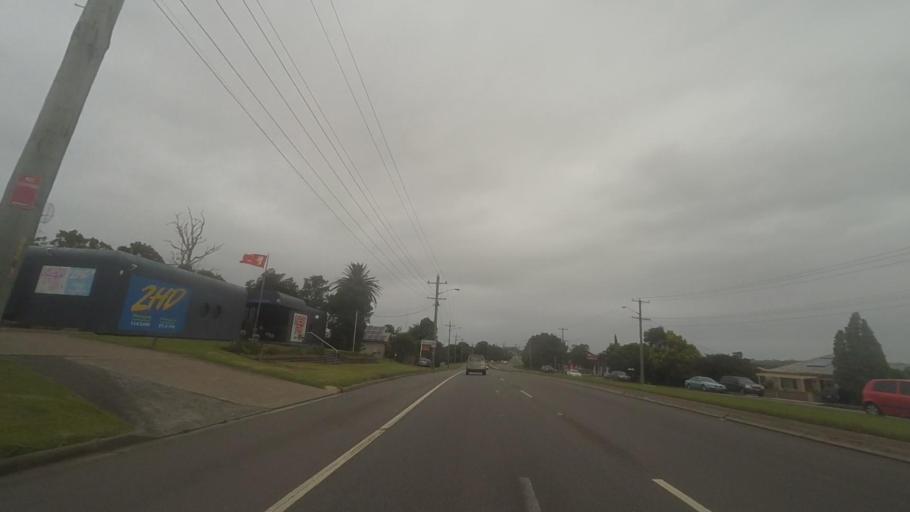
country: AU
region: New South Wales
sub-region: Newcastle
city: Mayfield West
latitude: -32.8640
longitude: 151.7059
